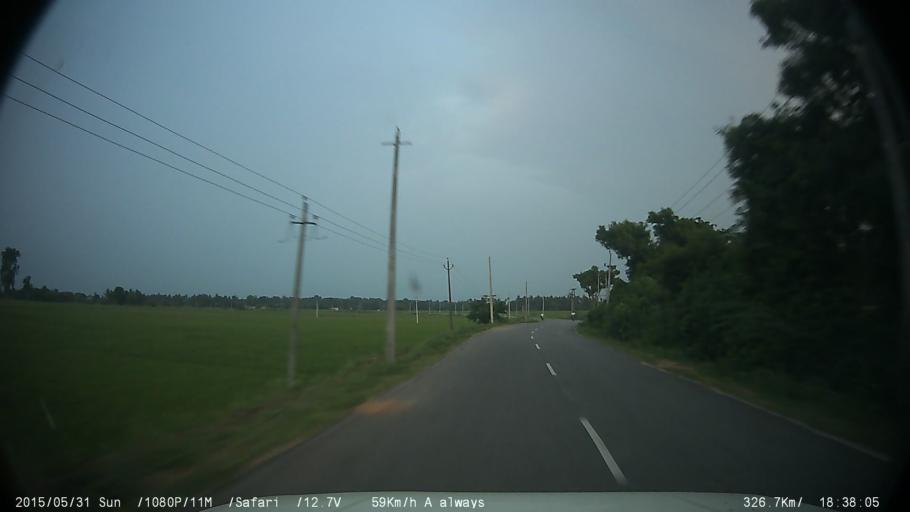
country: IN
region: Karnataka
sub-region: Mysore
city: Nanjangud
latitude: 12.1445
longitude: 76.7745
